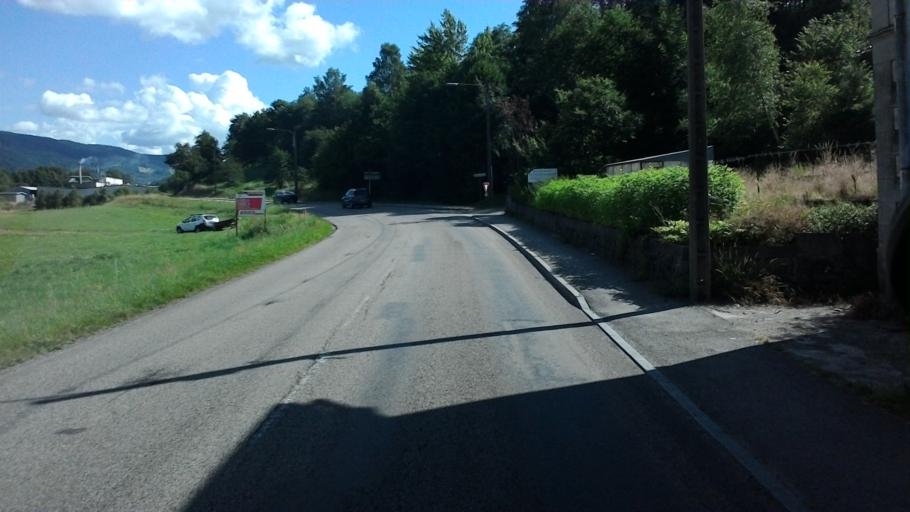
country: FR
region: Lorraine
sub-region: Departement des Vosges
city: Le Thillot
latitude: 47.8854
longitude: 6.7690
